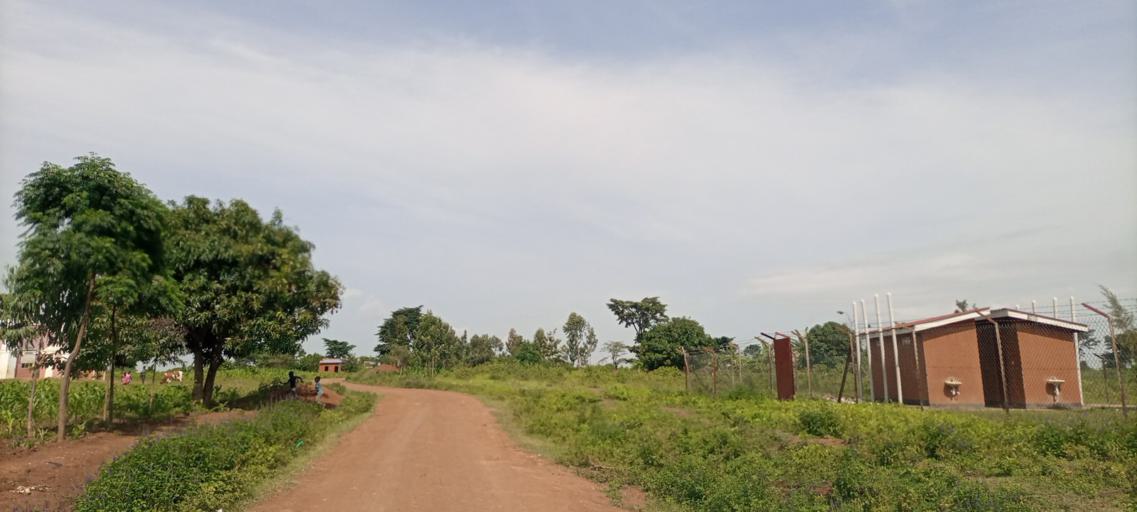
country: UG
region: Eastern Region
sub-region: Mbale District
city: Mbale
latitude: 1.1303
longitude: 34.0450
